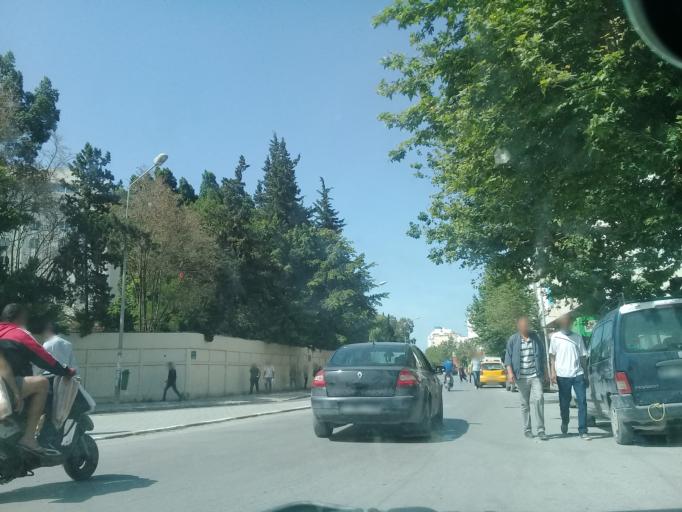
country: TN
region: Tunis
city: Tunis
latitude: 36.8127
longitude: 10.1746
